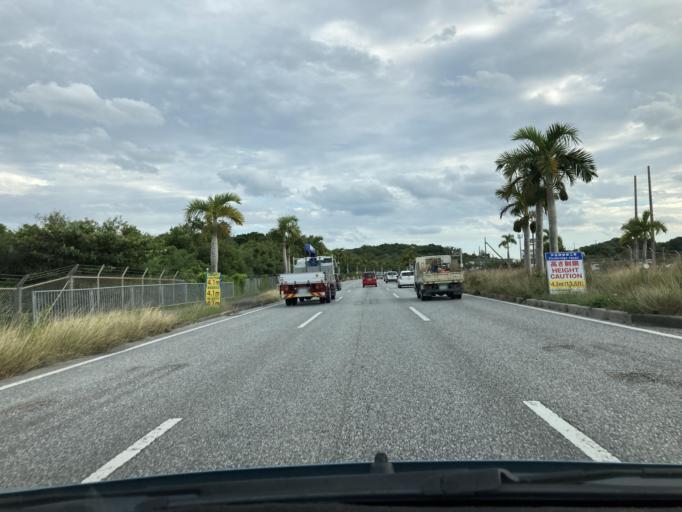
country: JP
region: Okinawa
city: Chatan
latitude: 26.3401
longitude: 127.7505
